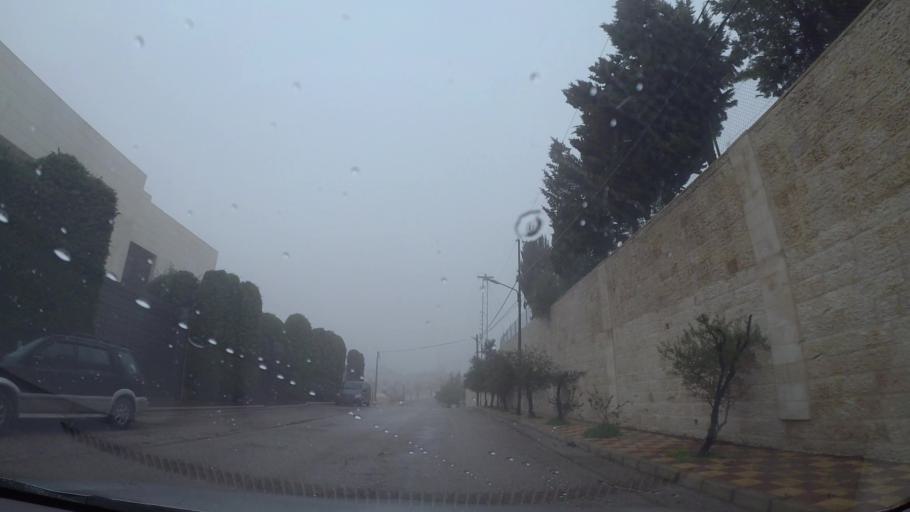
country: JO
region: Amman
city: Wadi as Sir
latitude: 31.9959
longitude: 35.8208
